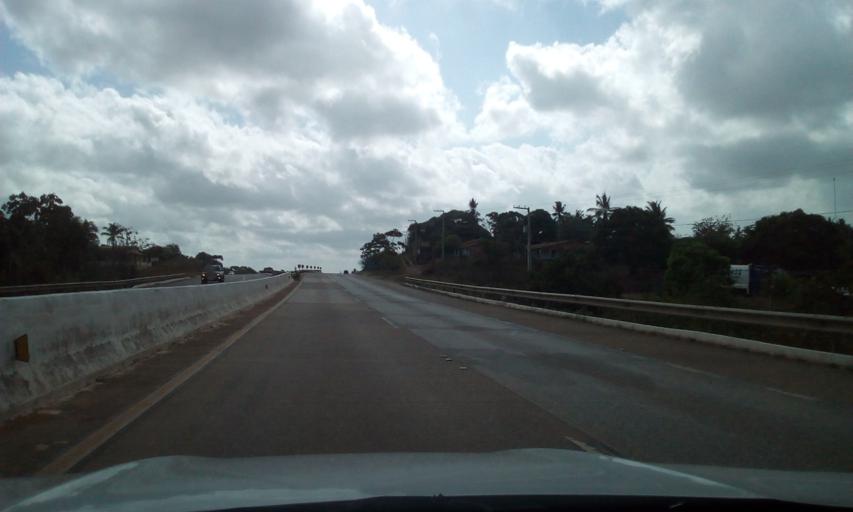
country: BR
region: Sergipe
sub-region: Sao Cristovao
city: Sao Cristovao
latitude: -10.9480
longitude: -37.2096
